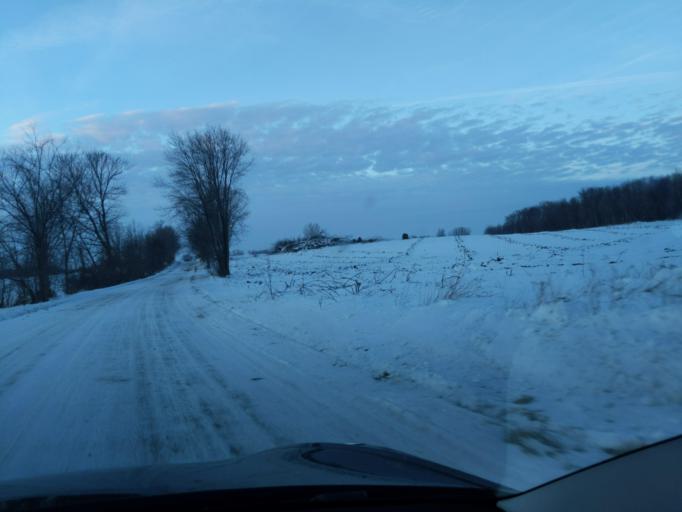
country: US
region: Michigan
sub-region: Ingham County
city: Williamston
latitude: 42.5678
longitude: -84.3124
